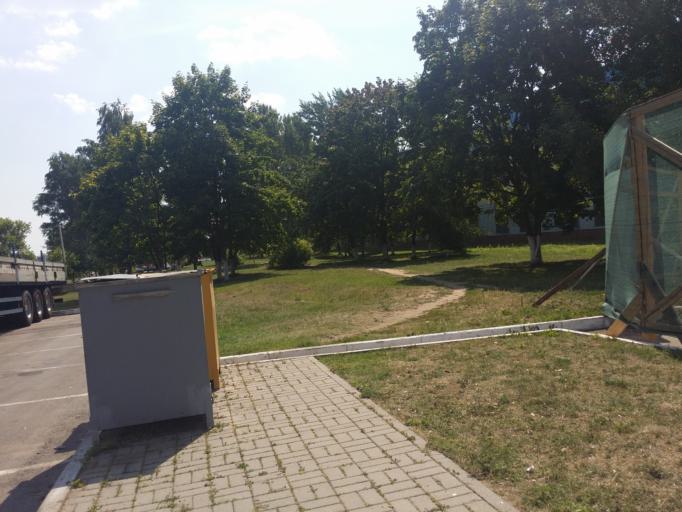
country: BY
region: Minsk
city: Vyaliki Trastsyanets
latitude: 53.8545
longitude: 27.6912
